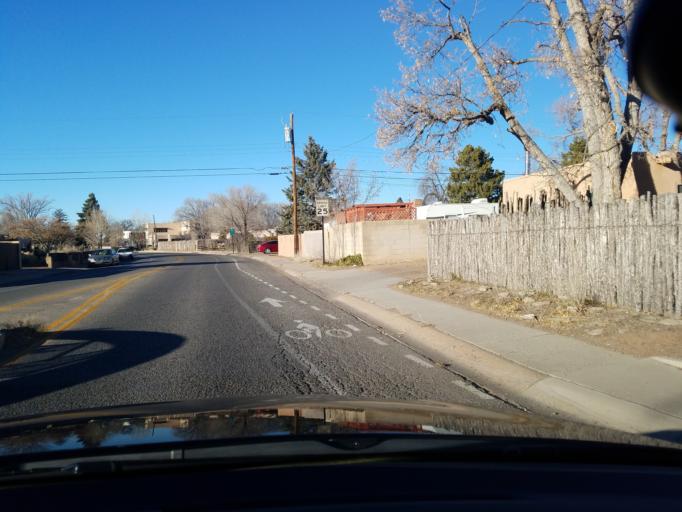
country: US
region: New Mexico
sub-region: Santa Fe County
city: Agua Fria
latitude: 35.6663
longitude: -105.9784
